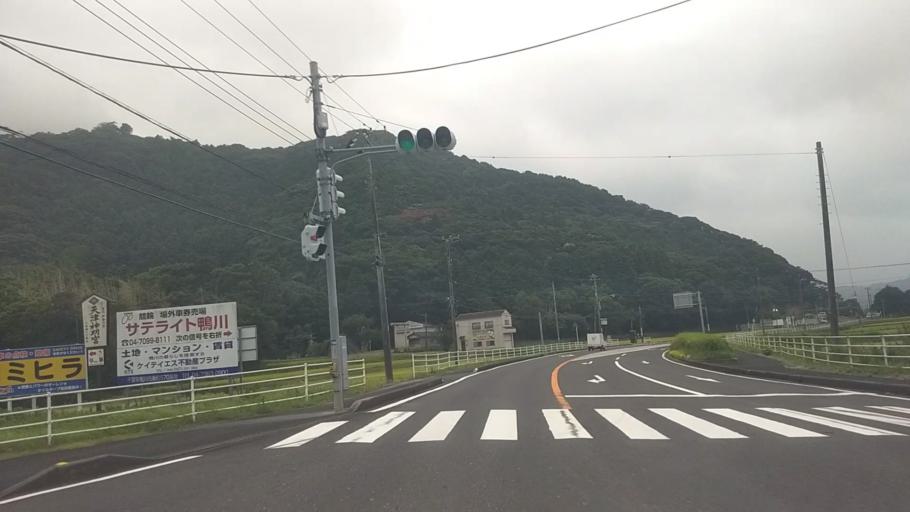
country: JP
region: Chiba
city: Kawaguchi
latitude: 35.1327
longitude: 140.0786
